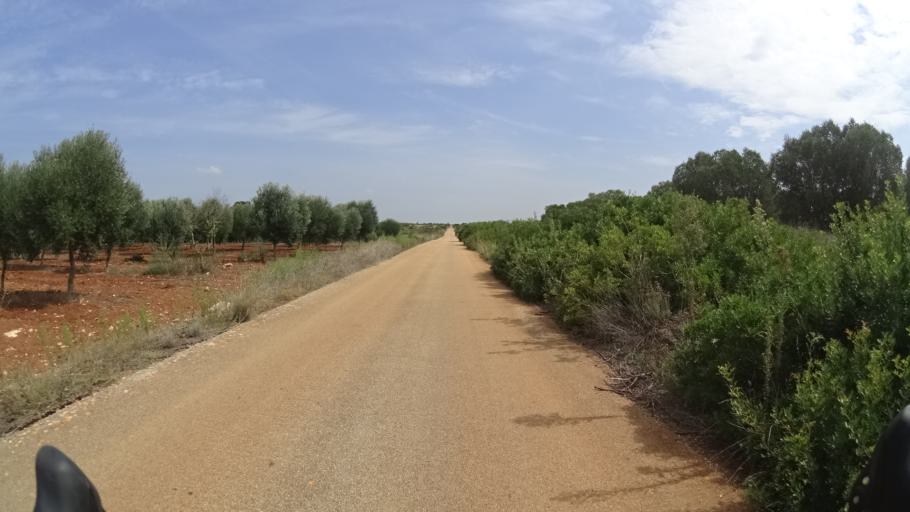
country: IT
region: Apulia
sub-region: Provincia di Taranto
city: Avetrana
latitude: 40.3490
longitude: 17.7972
